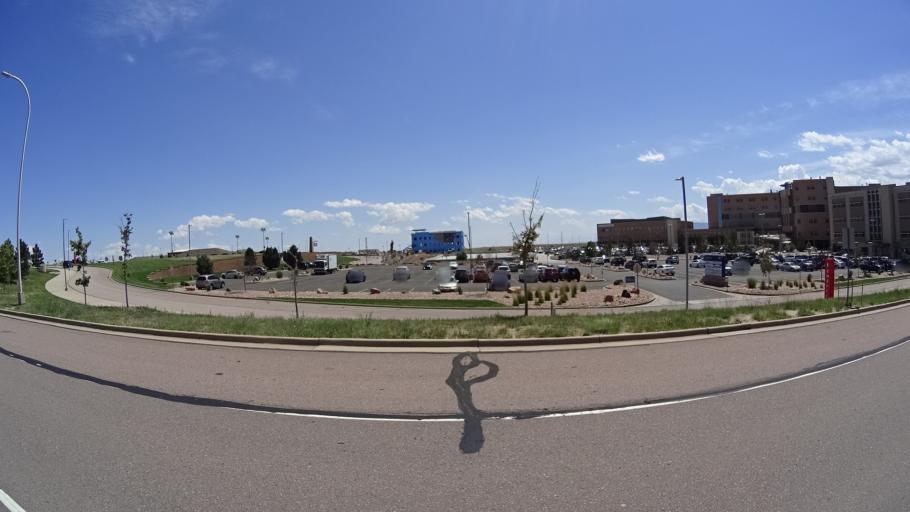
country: US
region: Colorado
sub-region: El Paso County
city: Black Forest
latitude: 38.9404
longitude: -104.7152
